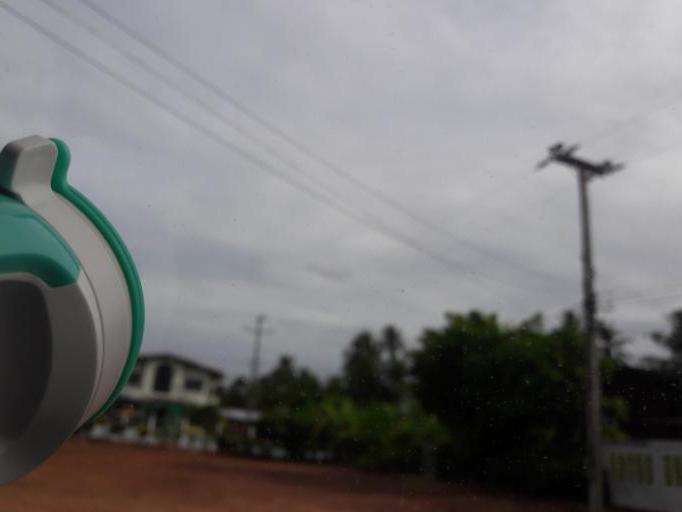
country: TH
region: Ratchaburi
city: Damnoen Saduak
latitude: 13.5188
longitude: 100.0016
